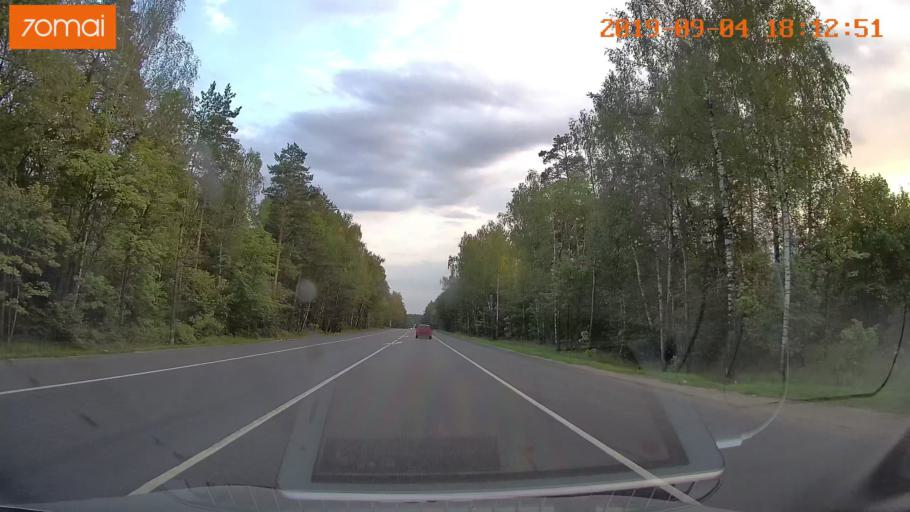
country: RU
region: Moskovskaya
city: Lopatinskiy
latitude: 55.3671
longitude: 38.7369
